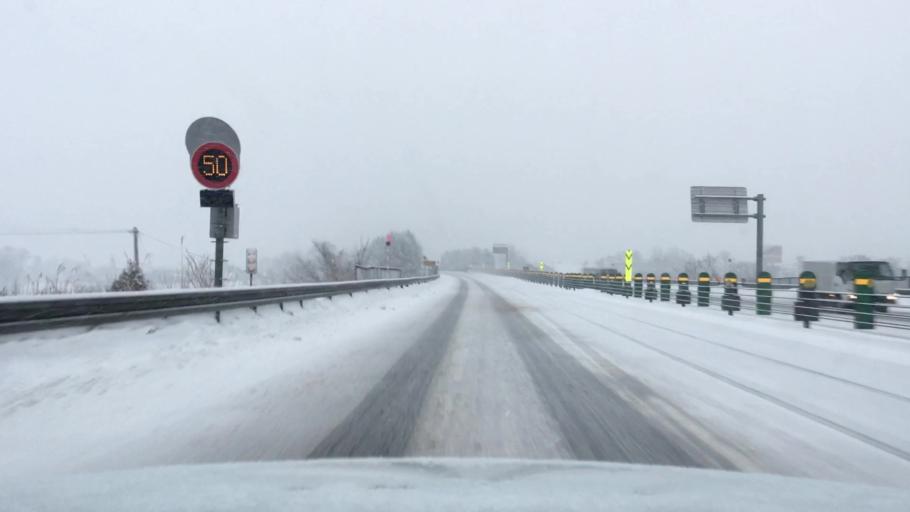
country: JP
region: Akita
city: Hanawa
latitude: 40.2584
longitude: 140.7669
